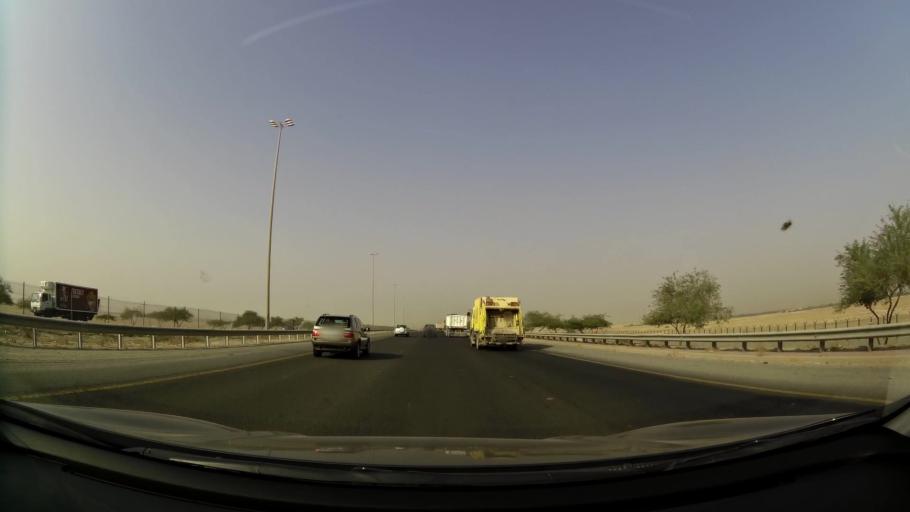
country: KW
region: Al Farwaniyah
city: Janub as Surrah
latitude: 29.1832
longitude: 47.9440
